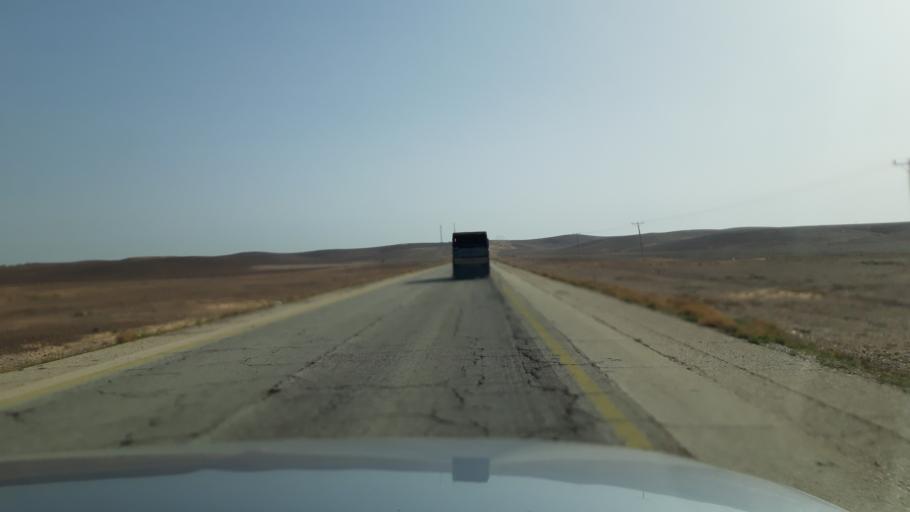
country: JO
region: Amman
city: Al Azraq ash Shamali
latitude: 31.8478
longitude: 36.6627
